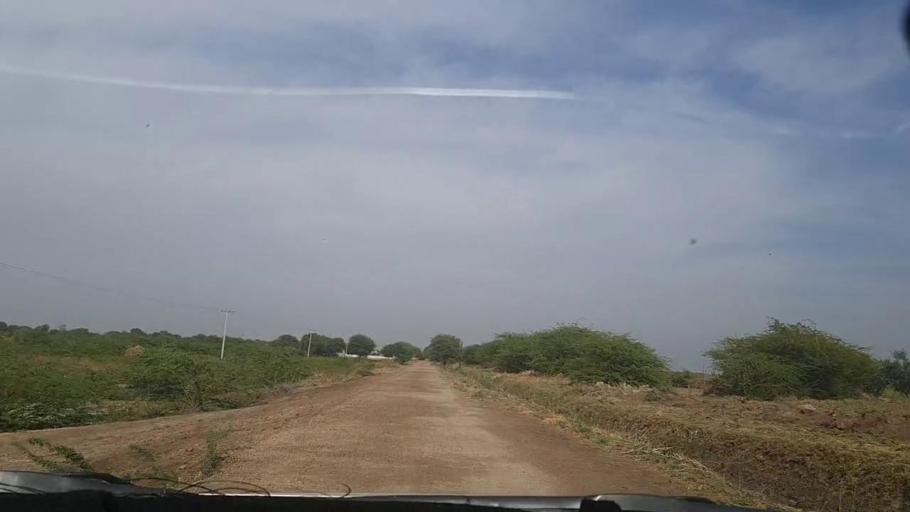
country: PK
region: Sindh
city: Pithoro
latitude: 25.5473
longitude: 69.3633
